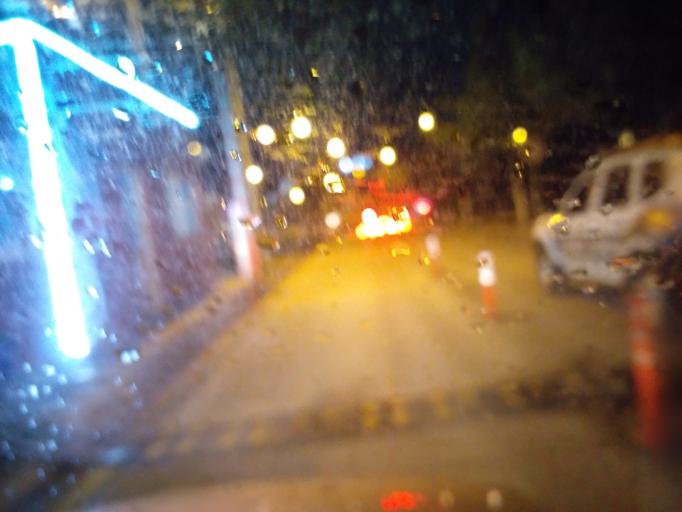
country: TR
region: Ankara
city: Batikent
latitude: 39.8801
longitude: 32.7121
